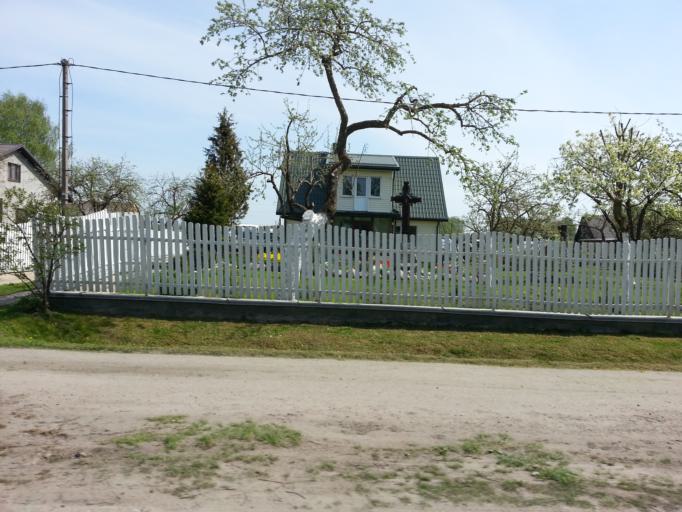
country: LT
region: Panevezys
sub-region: Panevezys City
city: Panevezys
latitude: 55.7641
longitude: 24.3009
